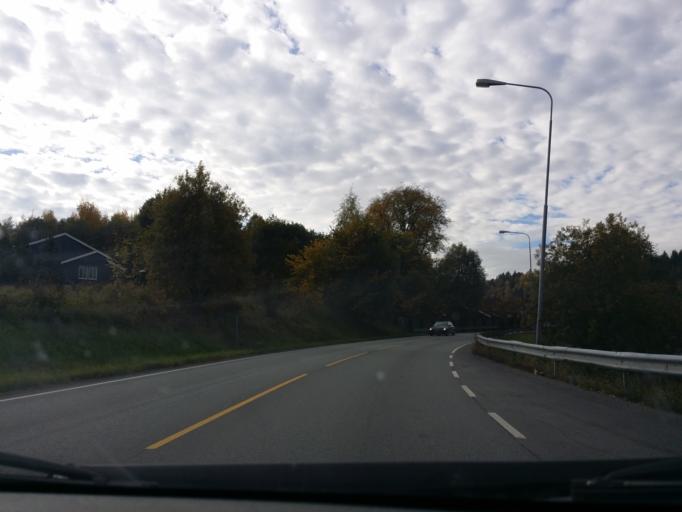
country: NO
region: Akershus
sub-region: Baerum
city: Sandvika
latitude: 59.9427
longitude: 10.5064
